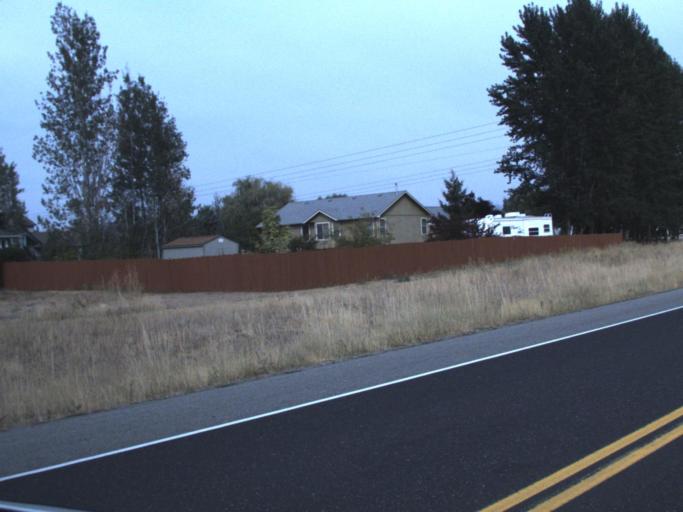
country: US
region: Washington
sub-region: Spokane County
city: Mead
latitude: 47.7873
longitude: -117.3326
